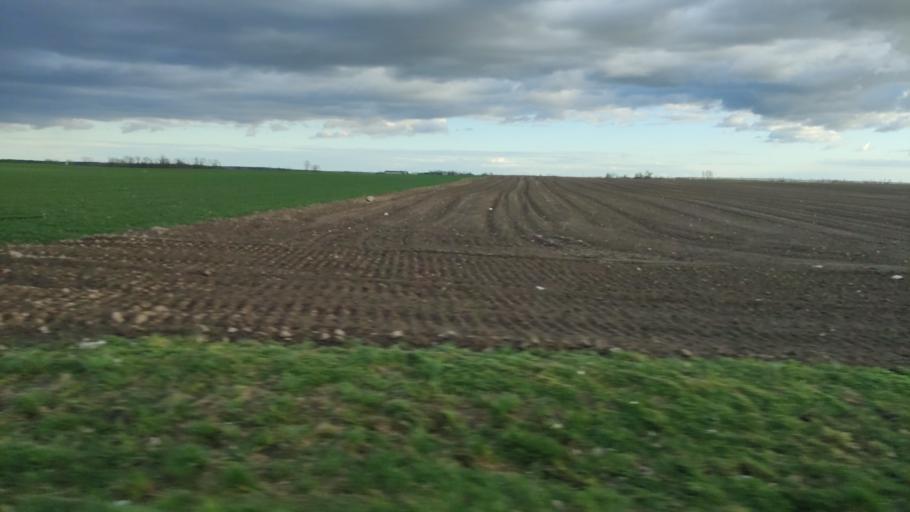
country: PL
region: Kujawsko-Pomorskie
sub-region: Powiat zninski
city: Znin
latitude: 52.8705
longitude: 17.8269
